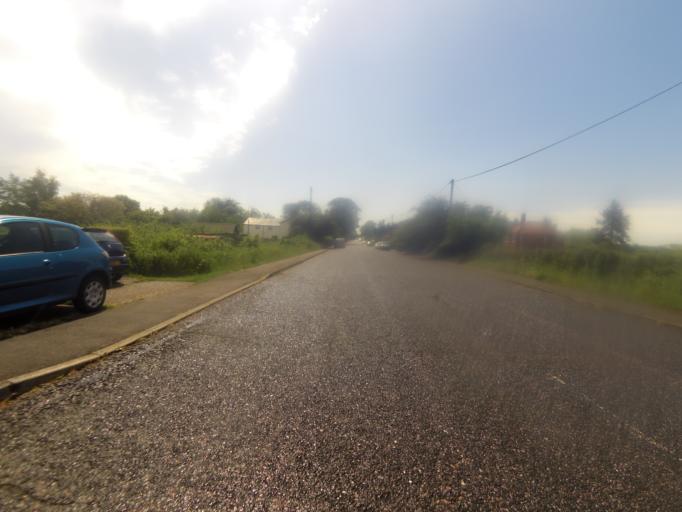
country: GB
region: England
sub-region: Suffolk
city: Bramford
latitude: 52.0884
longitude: 1.1224
